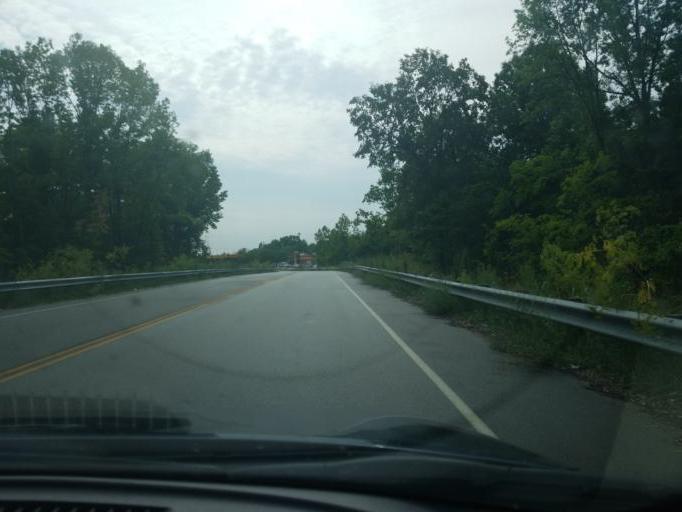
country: US
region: Kentucky
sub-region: Bullitt County
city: Shepherdsville
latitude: 37.9795
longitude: -85.6915
